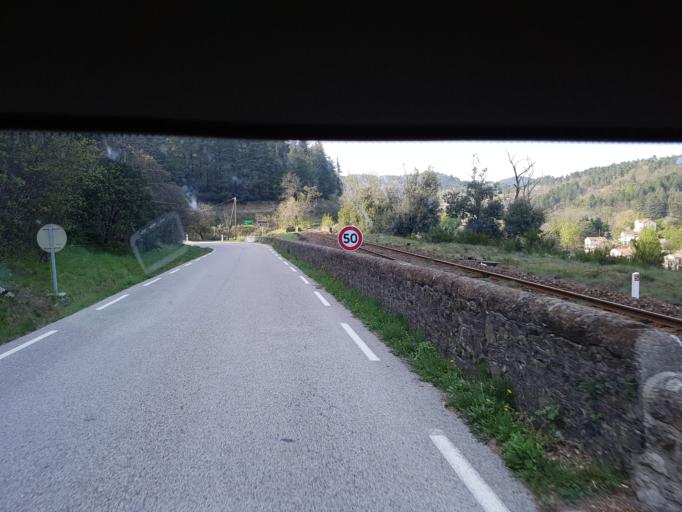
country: FR
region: Languedoc-Roussillon
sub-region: Departement du Gard
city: Branoux-les-Taillades
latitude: 44.3408
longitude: 3.9519
